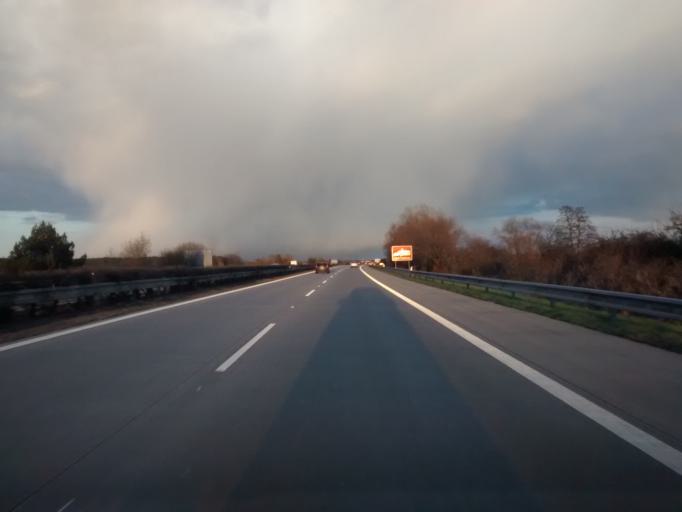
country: CZ
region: Central Bohemia
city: Pecky
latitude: 50.1235
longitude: 15.0349
